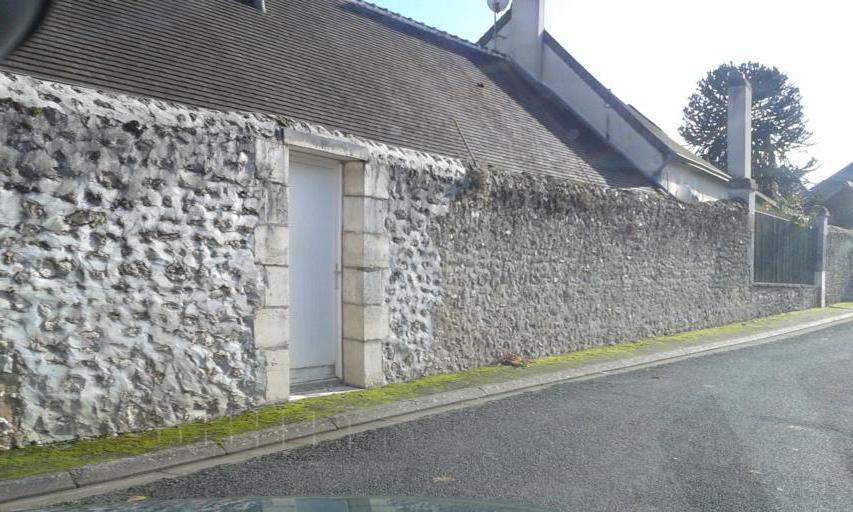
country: FR
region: Centre
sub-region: Departement du Loir-et-Cher
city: Mer
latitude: 47.7140
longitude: 1.5452
